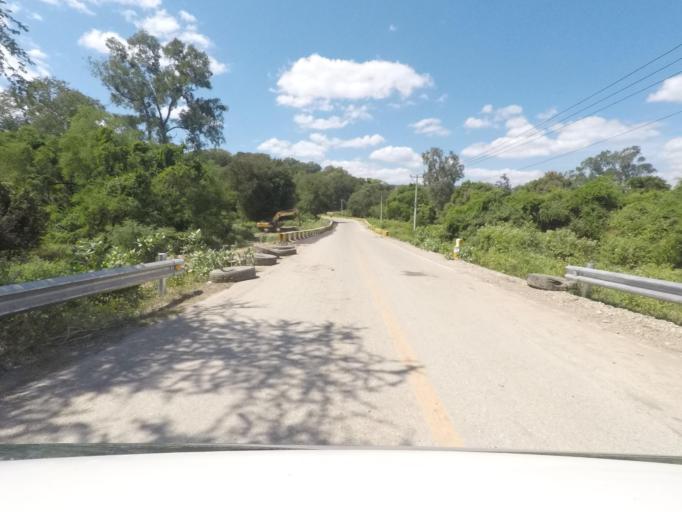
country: TL
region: Lautem
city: Lospalos
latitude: -8.3756
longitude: 126.8908
